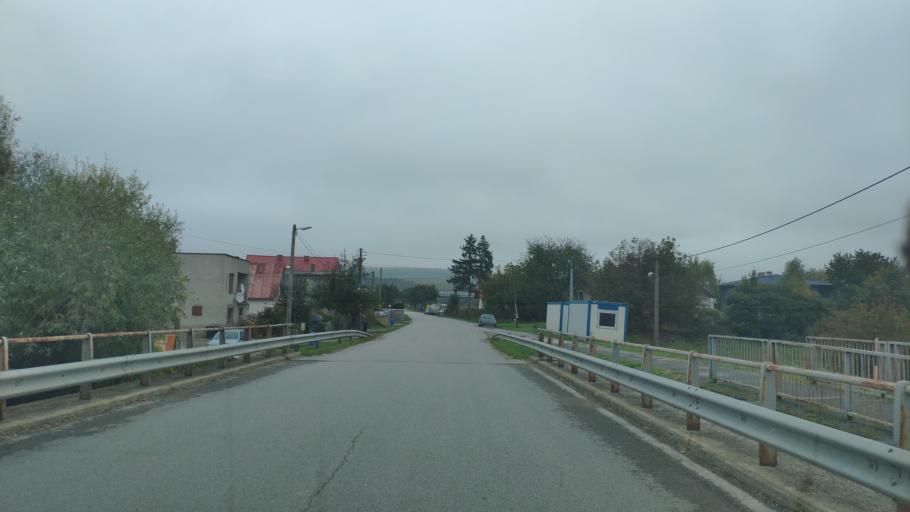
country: SK
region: Kosicky
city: Kosice
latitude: 48.7698
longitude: 21.3181
